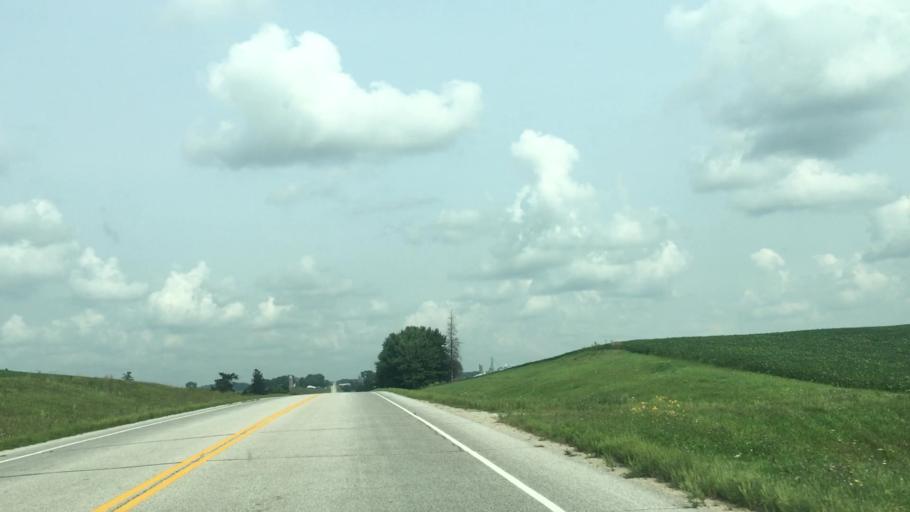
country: US
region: Minnesota
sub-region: Fillmore County
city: Harmony
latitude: 43.5999
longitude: -91.9297
